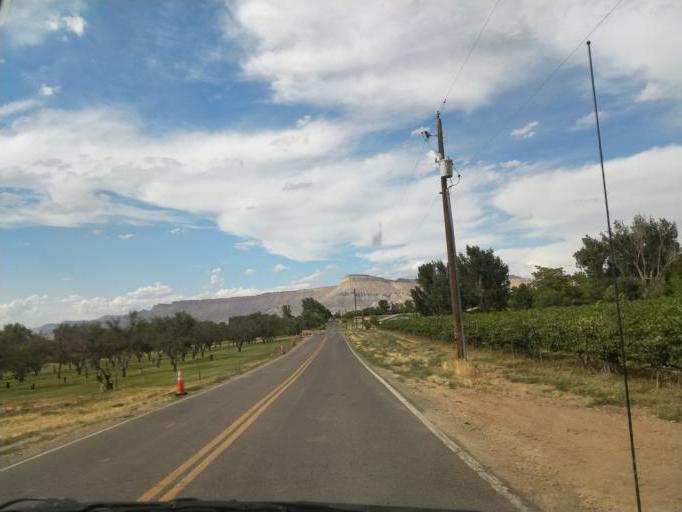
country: US
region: Colorado
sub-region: Mesa County
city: Clifton
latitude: 39.0581
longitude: -108.4133
